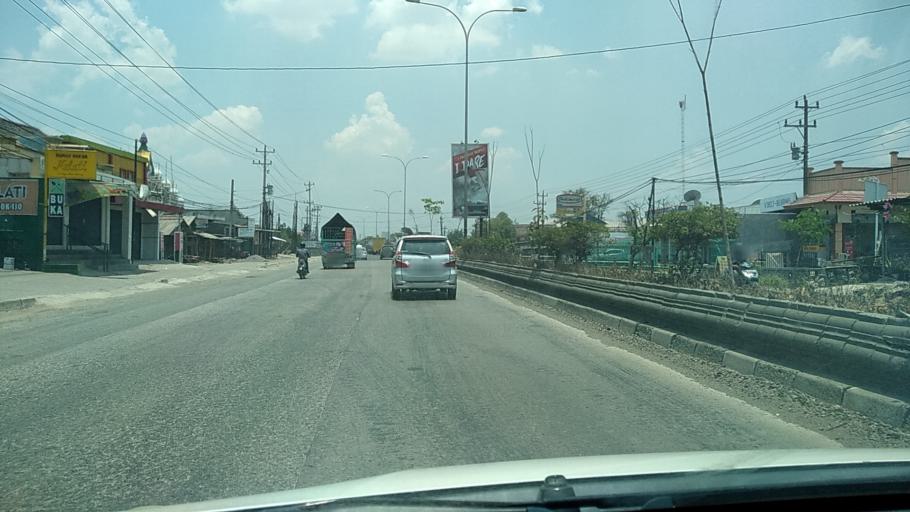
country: ID
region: Central Java
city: Semarang
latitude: -6.9550
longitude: 110.4710
